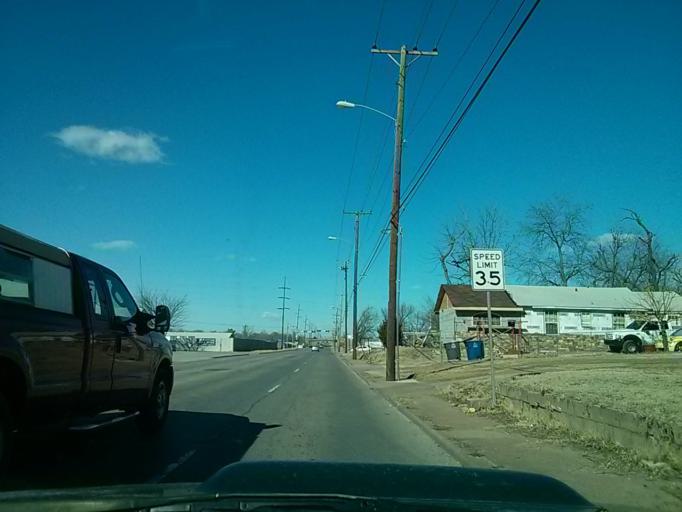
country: US
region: Oklahoma
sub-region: Tulsa County
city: Tulsa
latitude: 36.1845
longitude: -95.9582
